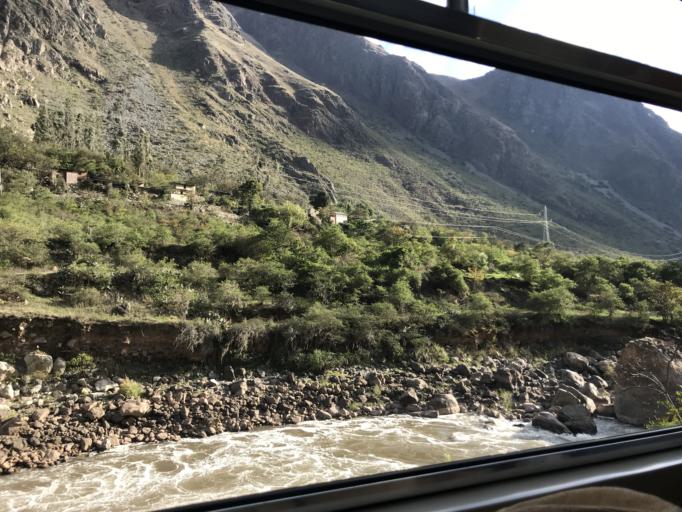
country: PE
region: Cusco
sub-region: Provincia de Urubamba
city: Ollantaytambo
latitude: -13.2268
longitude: -72.4020
